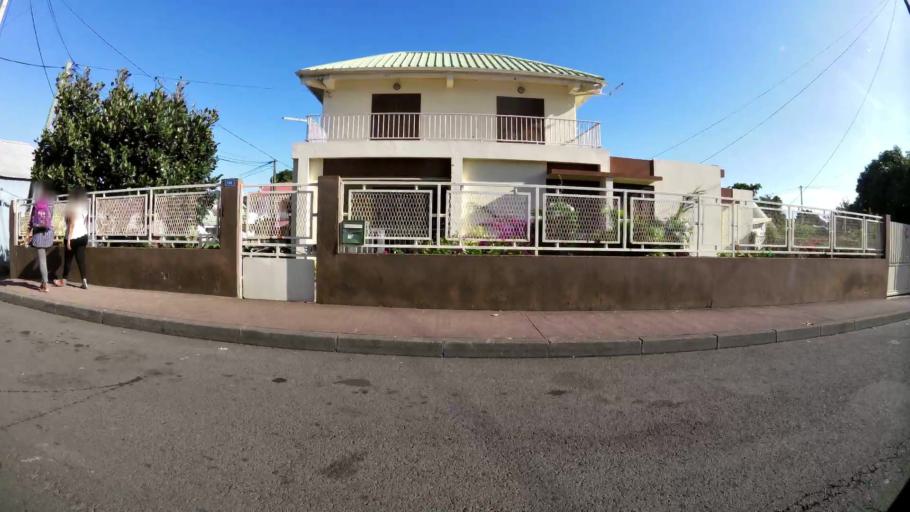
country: RE
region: Reunion
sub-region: Reunion
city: Saint-Louis
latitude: -21.2874
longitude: 55.4153
